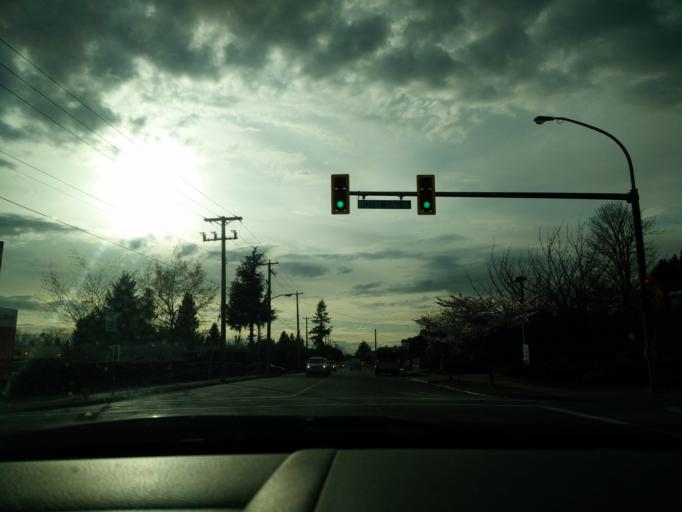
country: CA
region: British Columbia
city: Burnaby
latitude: 49.2150
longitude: -122.9884
